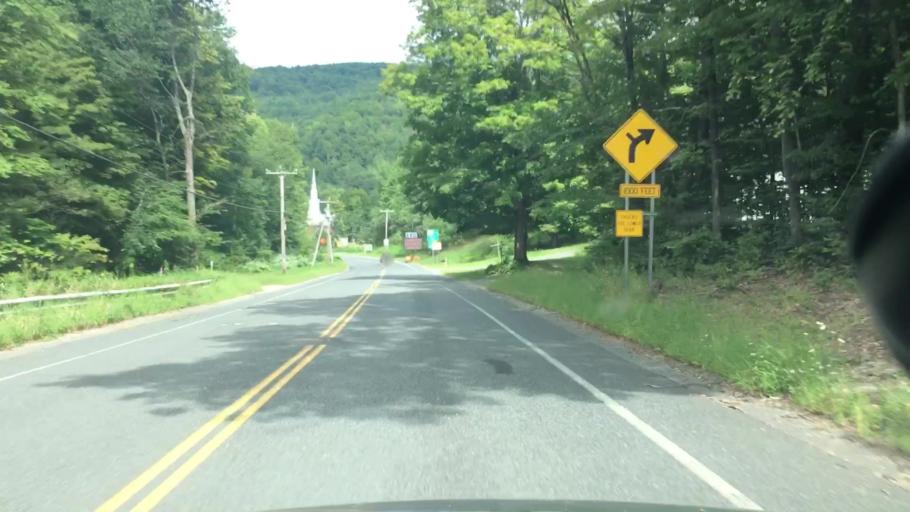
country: US
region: Massachusetts
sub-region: Franklin County
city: Colrain
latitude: 42.6702
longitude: -72.6941
